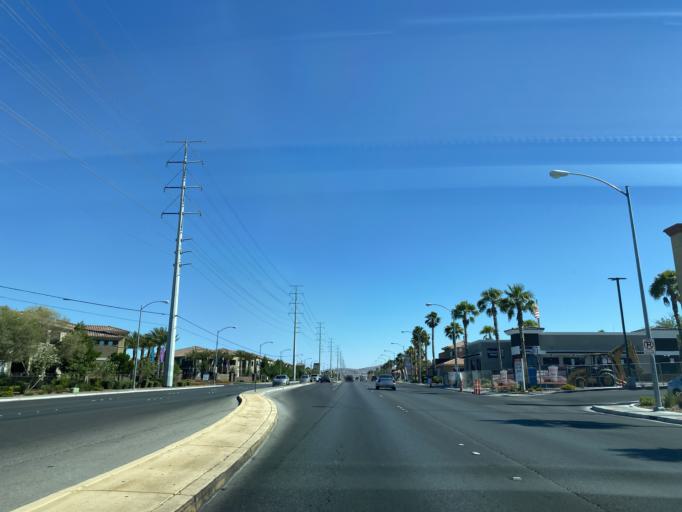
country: US
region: Nevada
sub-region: Clark County
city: Enterprise
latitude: 36.0477
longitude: -115.2435
